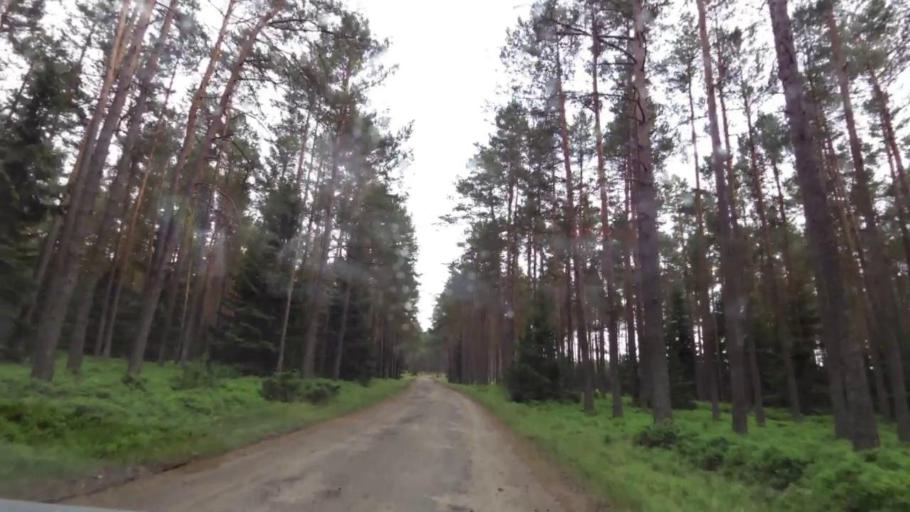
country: PL
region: Pomeranian Voivodeship
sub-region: Powiat bytowski
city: Trzebielino
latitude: 54.2105
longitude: 17.0048
